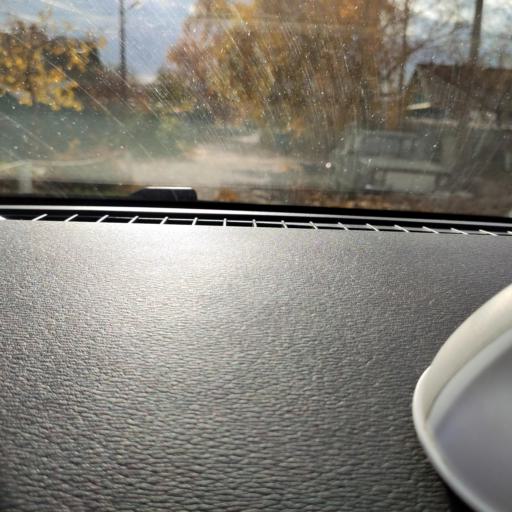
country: RU
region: Samara
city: Petra-Dubrava
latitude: 53.2518
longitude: 50.3126
